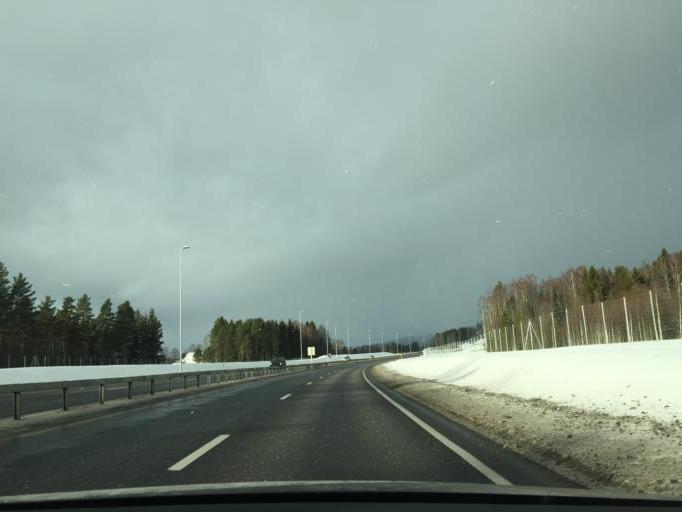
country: NO
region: Hedmark
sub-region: Kongsvinger
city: Spetalen
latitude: 60.2148
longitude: 11.8735
